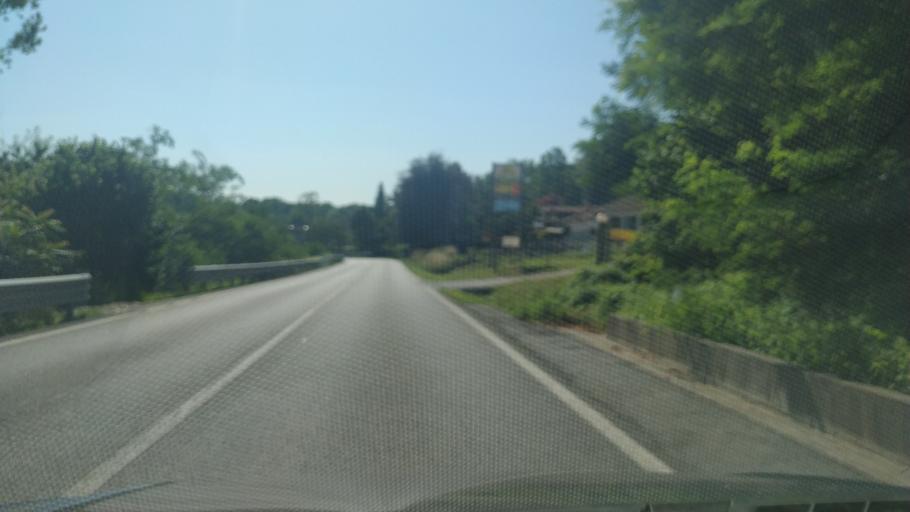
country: IT
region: Piedmont
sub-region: Provincia di Novara
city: Cureggio
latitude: 45.6685
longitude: 8.4496
